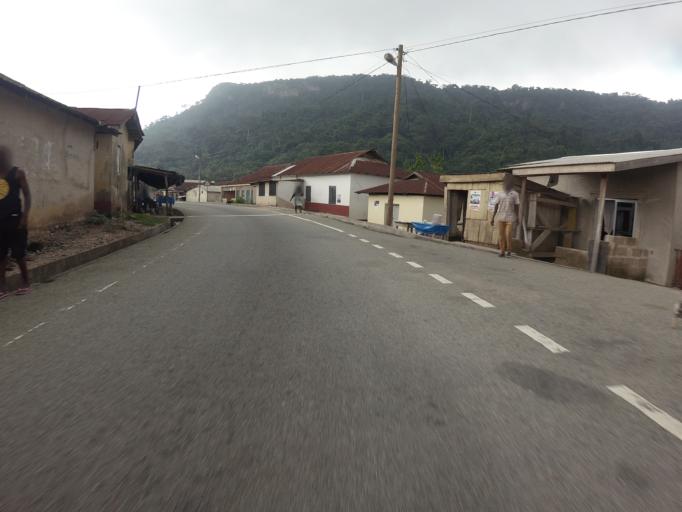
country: GH
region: Volta
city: Kpandu
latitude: 6.8219
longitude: 0.4252
